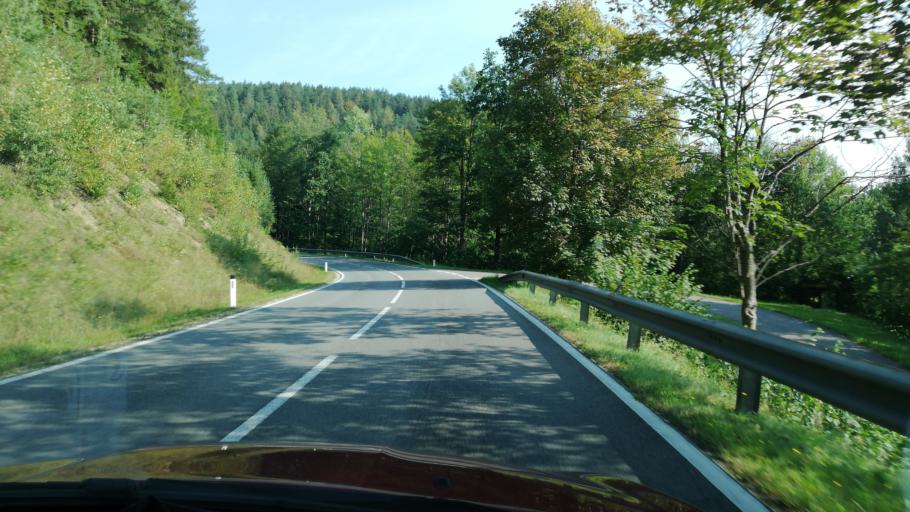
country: AT
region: Upper Austria
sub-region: Politischer Bezirk Perg
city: Sankt Georgen am Walde
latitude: 48.4181
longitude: 14.7634
